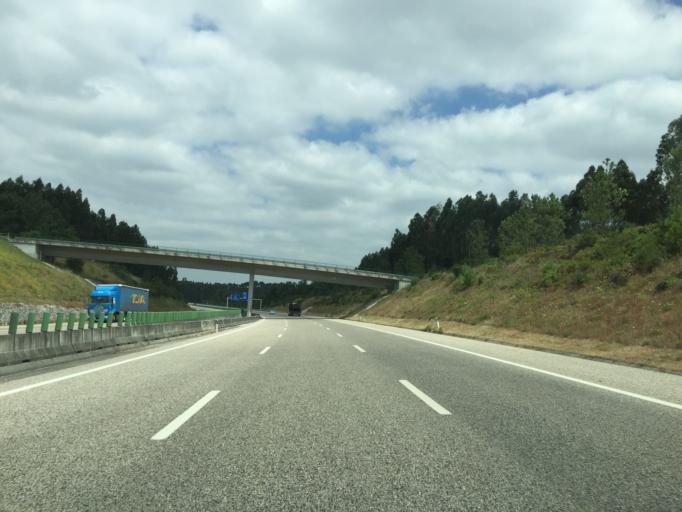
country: PT
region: Leiria
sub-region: Pombal
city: Lourical
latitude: 39.9763
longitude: -8.7826
